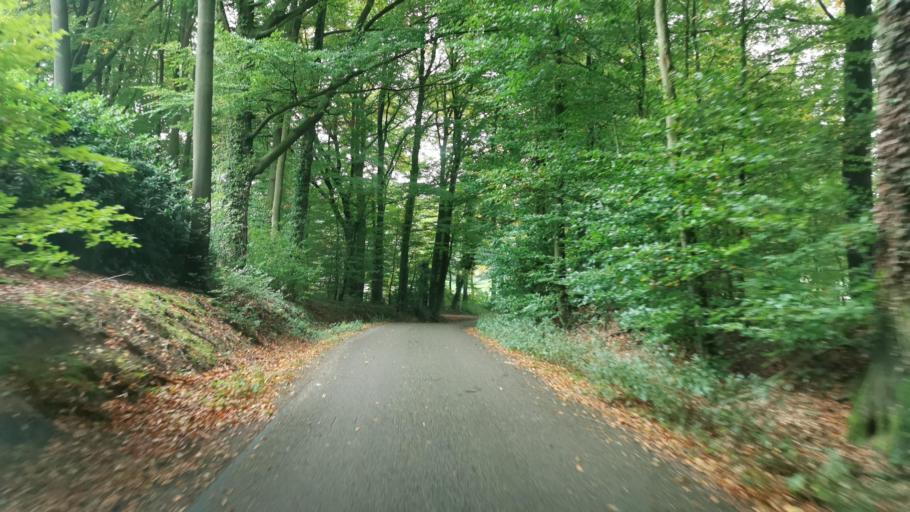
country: NL
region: Overijssel
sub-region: Gemeente Oldenzaal
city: Oldenzaal
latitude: 52.3280
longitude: 6.9720
